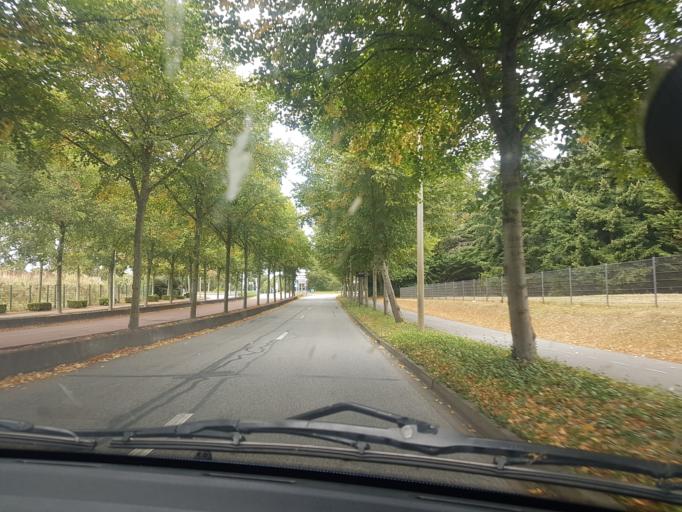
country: FR
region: Ile-de-France
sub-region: Departement des Yvelines
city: Guyancourt
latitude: 48.7606
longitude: 2.0734
